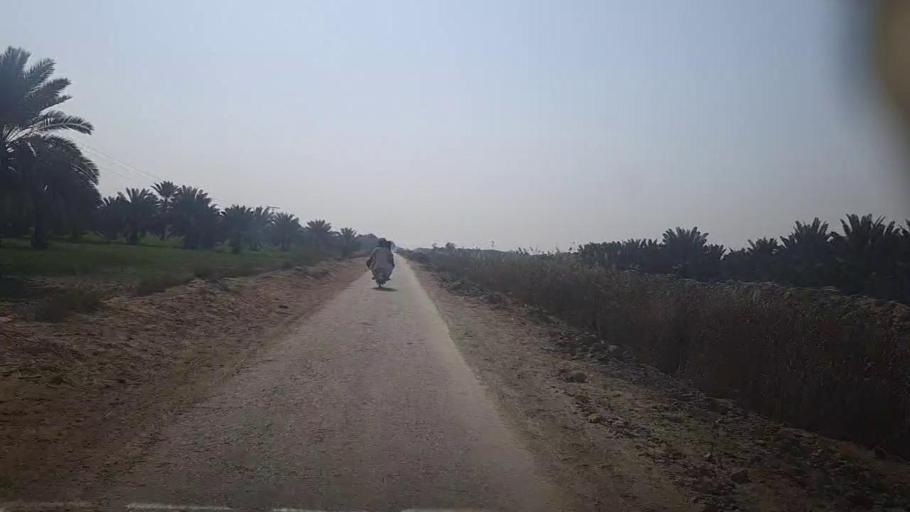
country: PK
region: Sindh
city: Khairpur
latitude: 27.4579
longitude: 68.8150
